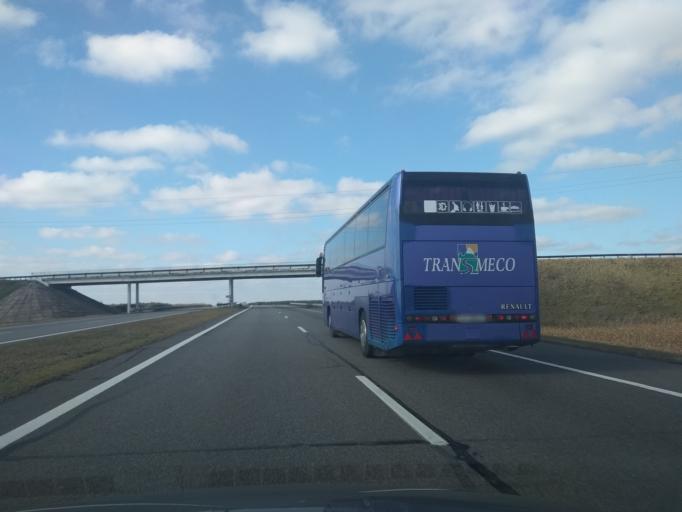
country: BY
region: Minsk
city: Stowbtsy
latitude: 53.5363
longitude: 26.8049
